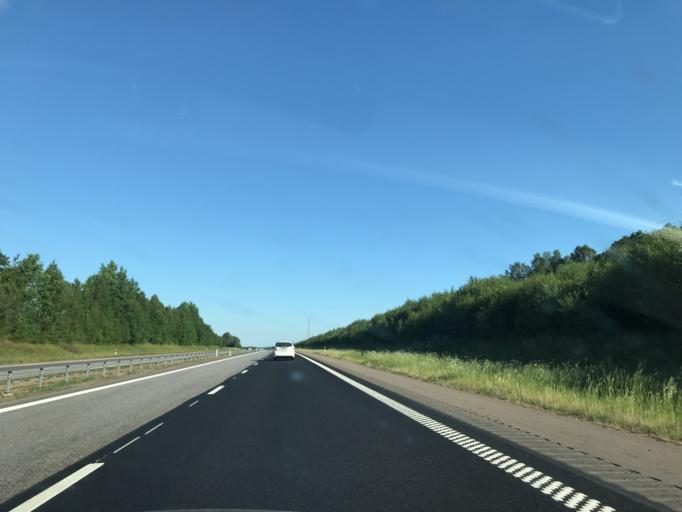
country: SE
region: Halland
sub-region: Halmstads Kommun
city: Aled
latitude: 56.7448
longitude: 12.8646
